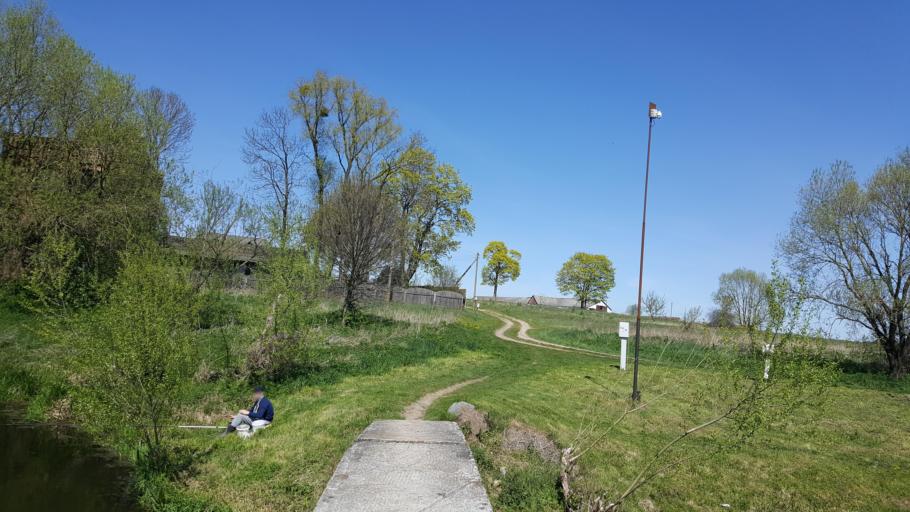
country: BY
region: Brest
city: Kamyanyets
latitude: 52.4374
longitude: 23.8478
